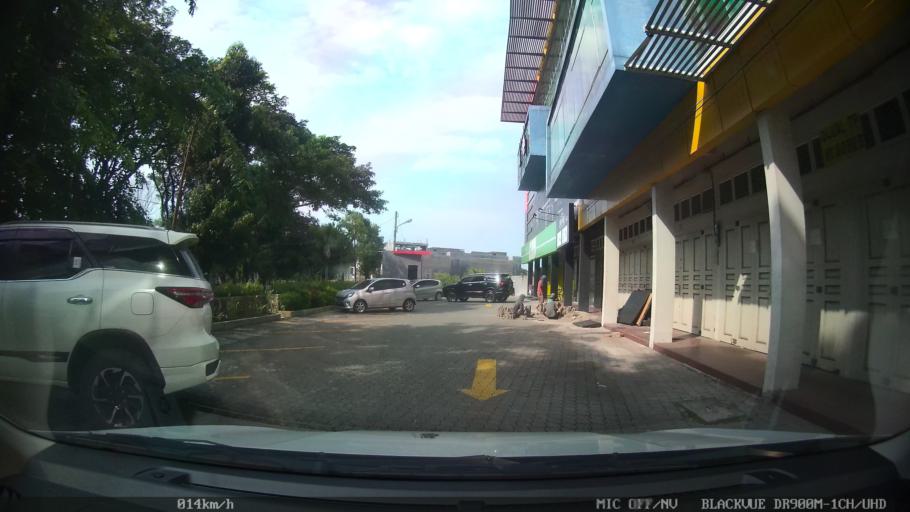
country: ID
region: North Sumatra
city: Medan
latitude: 3.5593
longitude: 98.6836
